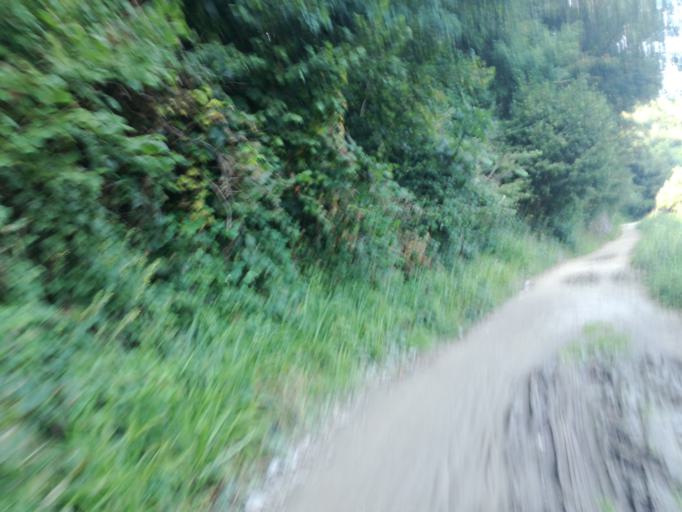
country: IT
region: Lombardy
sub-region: Provincia di Lecco
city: Imbersago
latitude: 45.7128
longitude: 9.4493
